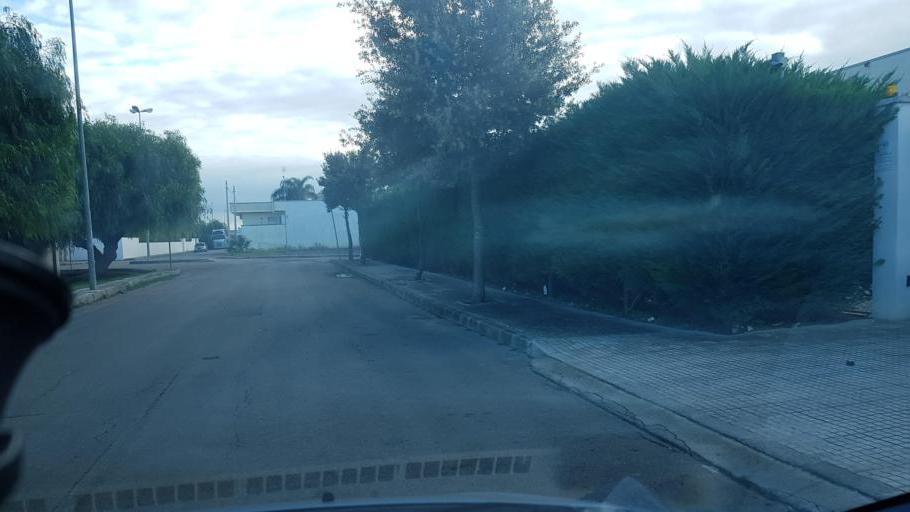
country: IT
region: Apulia
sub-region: Provincia di Lecce
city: Veglie
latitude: 40.3455
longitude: 17.9706
